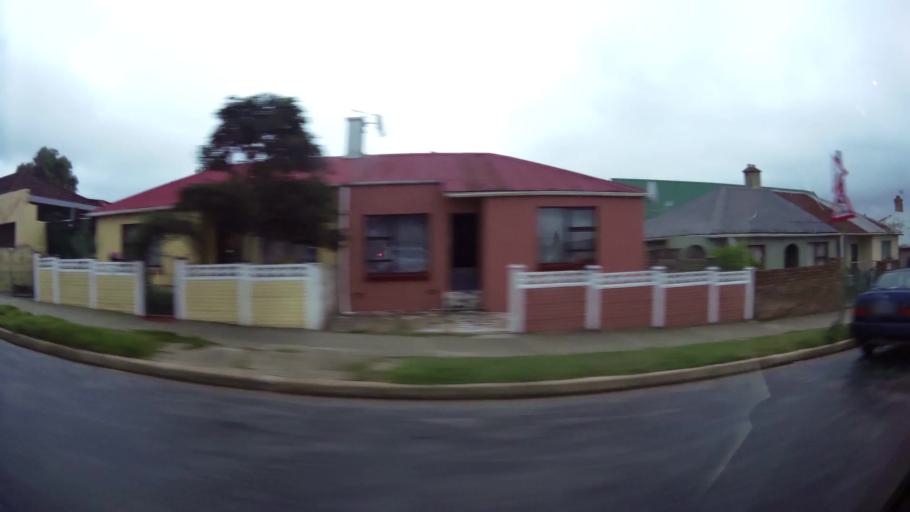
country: ZA
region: Eastern Cape
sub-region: Nelson Mandela Bay Metropolitan Municipality
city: Port Elizabeth
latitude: -33.9394
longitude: 25.5931
